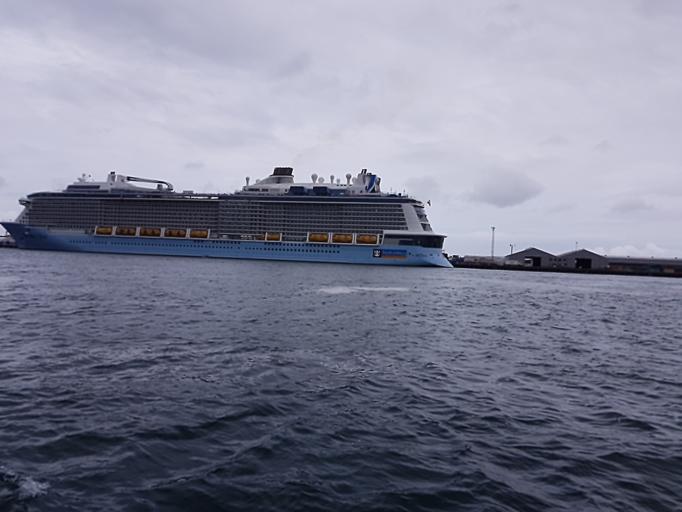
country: NZ
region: Bay of Plenty
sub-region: Tauranga City
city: Tauranga
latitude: -37.6458
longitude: 176.1782
